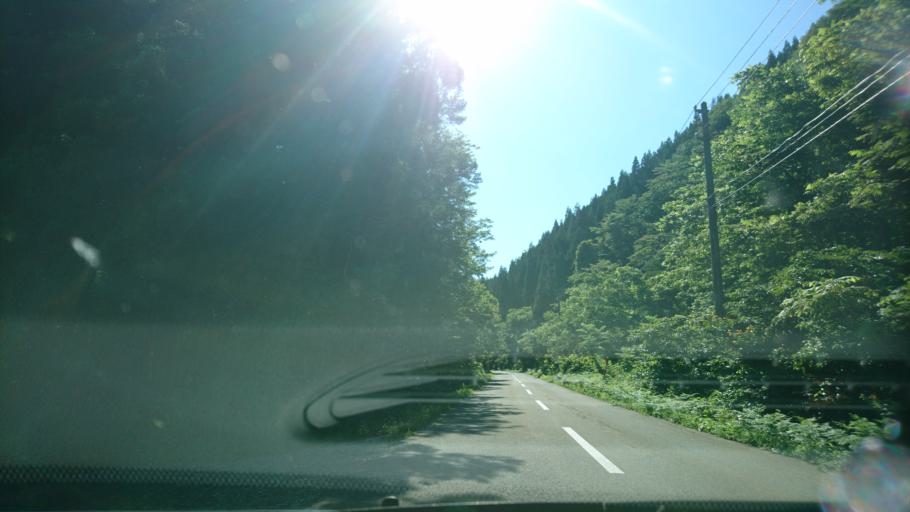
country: JP
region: Akita
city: Kakunodatemachi
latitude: 39.7070
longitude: 140.5993
